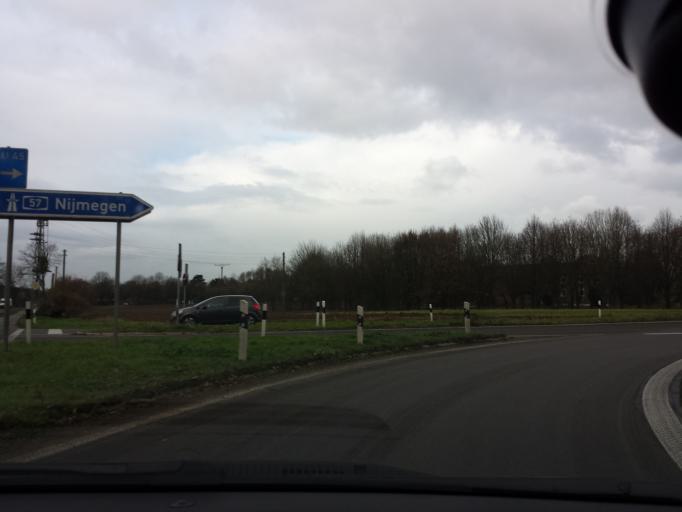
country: DE
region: North Rhine-Westphalia
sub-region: Regierungsbezirk Dusseldorf
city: Goch
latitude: 51.6563
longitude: 6.1800
